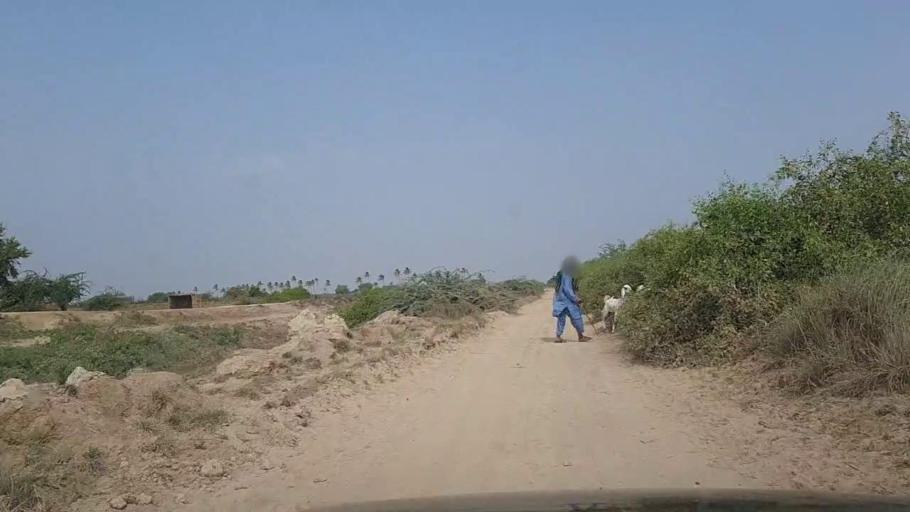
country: PK
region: Sindh
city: Thatta
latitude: 24.7551
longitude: 67.8093
